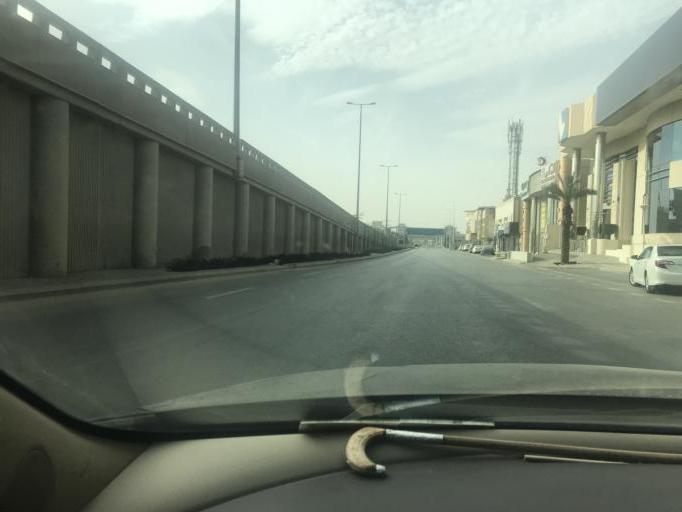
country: SA
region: Ar Riyad
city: Riyadh
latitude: 24.7766
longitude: 46.6653
